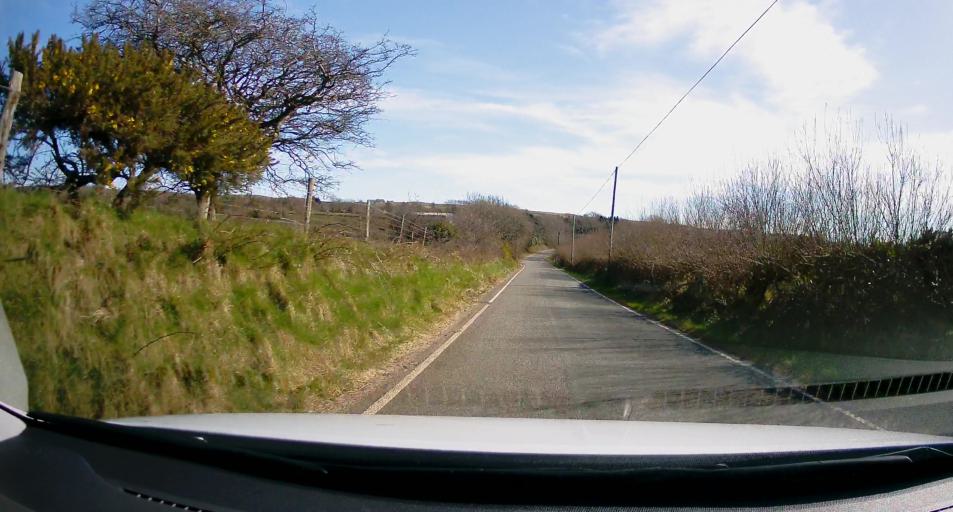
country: GB
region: Wales
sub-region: County of Ceredigion
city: Lledrod
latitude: 52.2926
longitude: -4.0672
